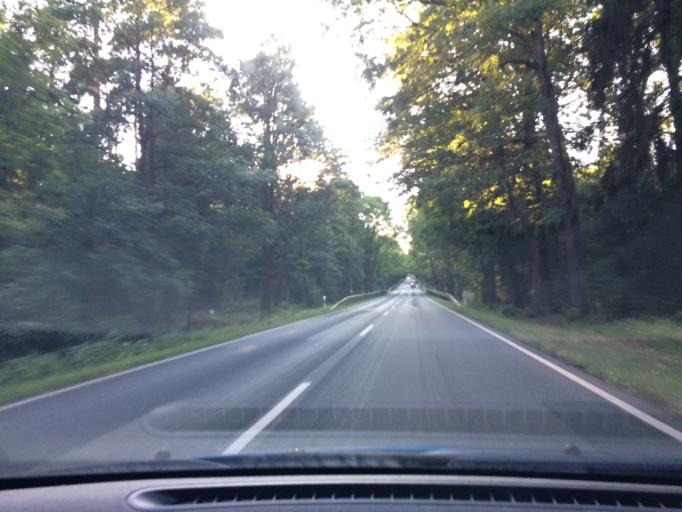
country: DE
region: Lower Saxony
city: Unterluss
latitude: 52.8083
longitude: 10.3619
